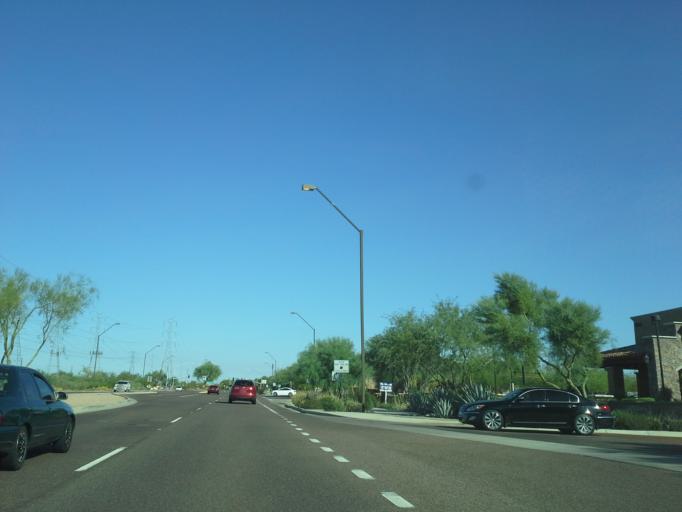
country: US
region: Arizona
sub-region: Maricopa County
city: Paradise Valley
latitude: 33.6693
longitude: -111.9053
